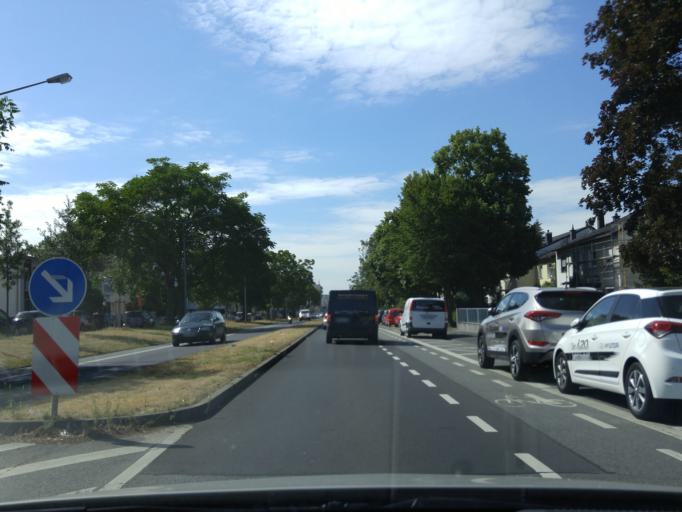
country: DE
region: Hesse
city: Dreieich
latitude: 50.0281
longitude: 8.6954
